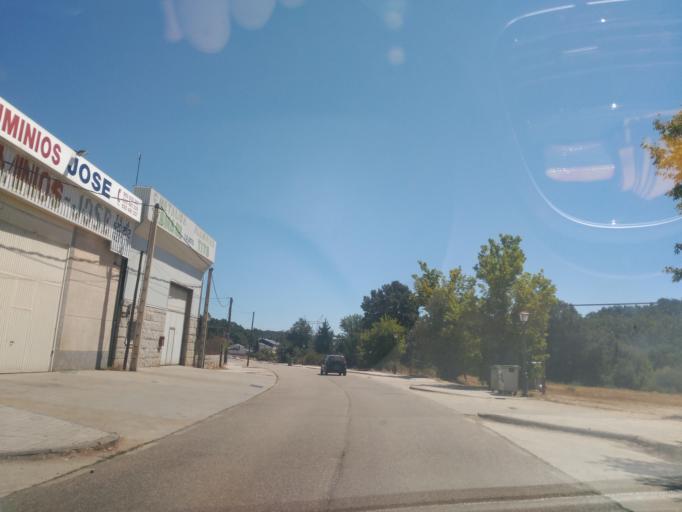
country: ES
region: Castille and Leon
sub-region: Provincia de Zamora
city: Galende
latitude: 42.0854
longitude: -6.6523
